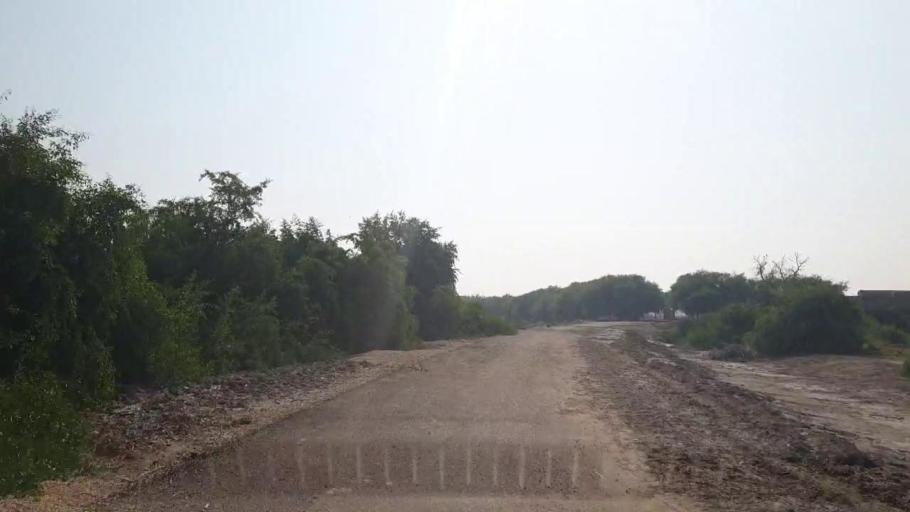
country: PK
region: Sindh
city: Sehwan
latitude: 26.4312
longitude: 67.7564
